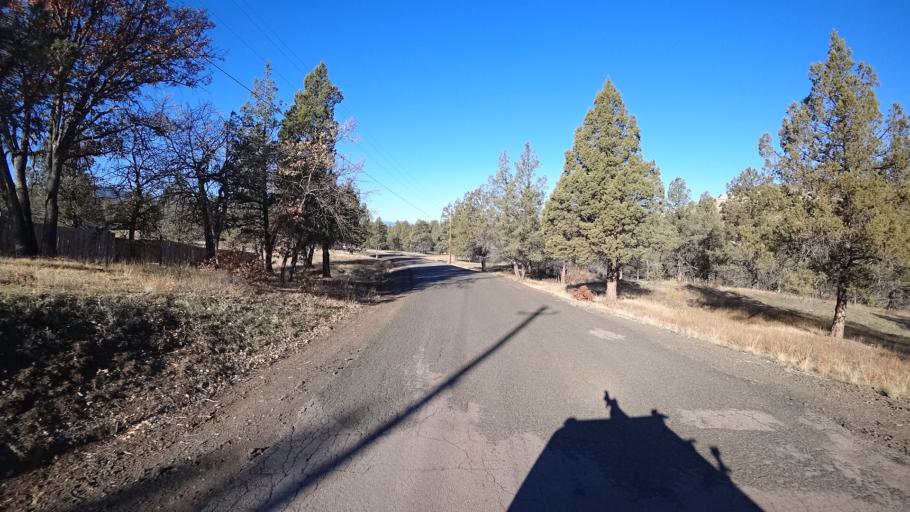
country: US
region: California
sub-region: Siskiyou County
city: Montague
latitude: 41.8902
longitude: -122.4351
